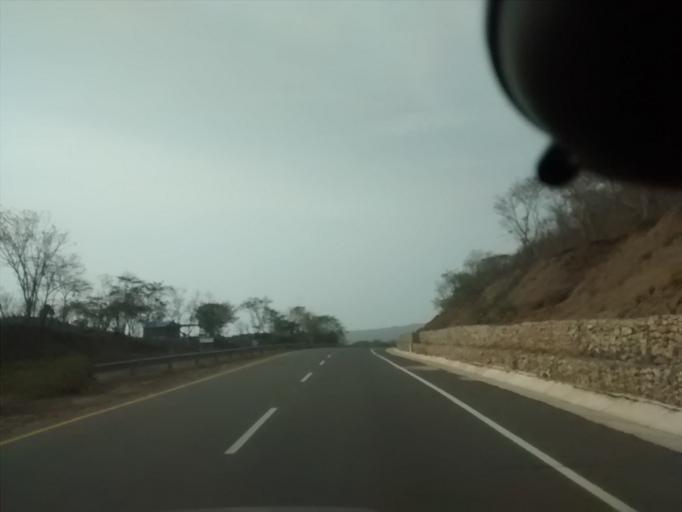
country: CO
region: Bolivar
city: Clemencia
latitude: 10.5767
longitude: -75.4500
